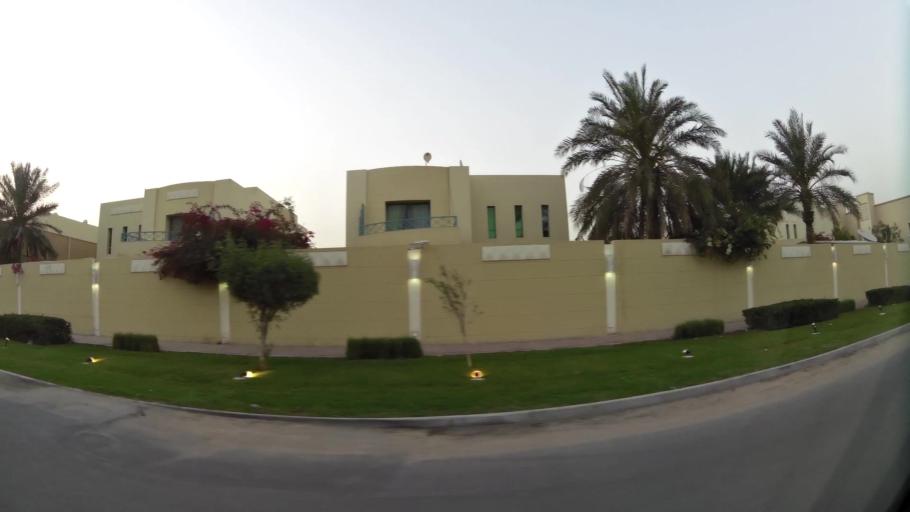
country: QA
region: Baladiyat ar Rayyan
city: Ar Rayyan
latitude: 25.2521
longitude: 51.4610
